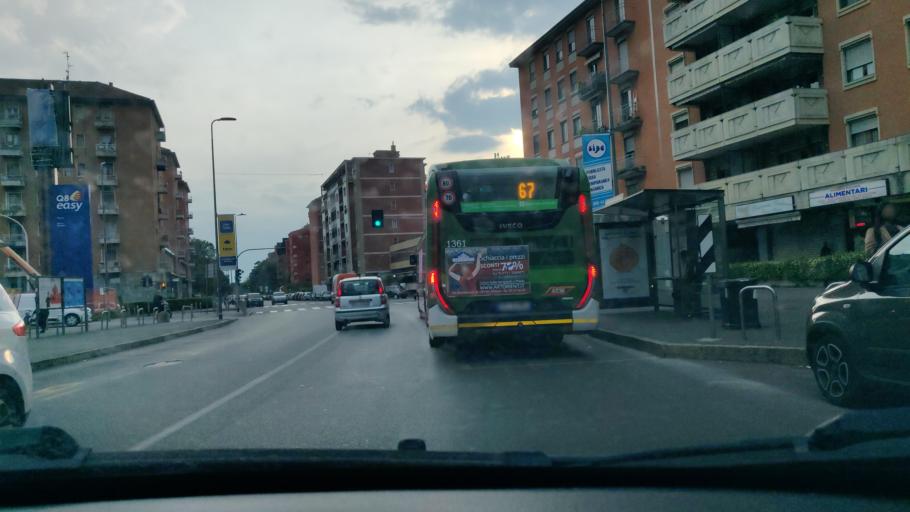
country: IT
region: Lombardy
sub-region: Citta metropolitana di Milano
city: Cesano Boscone
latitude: 45.4606
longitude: 9.1099
